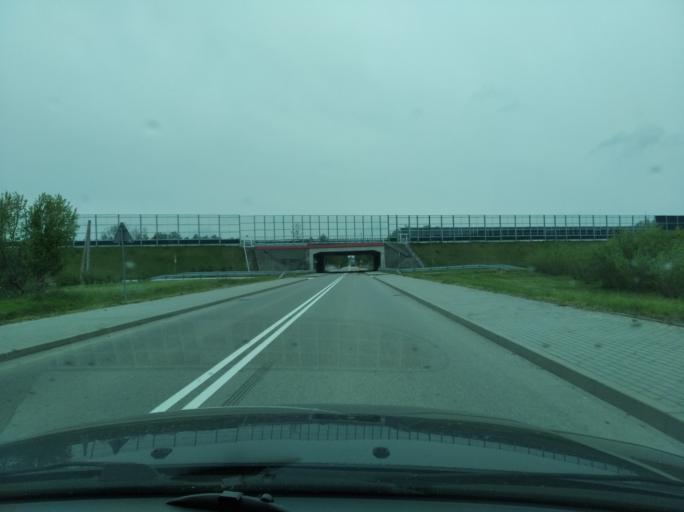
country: PL
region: Subcarpathian Voivodeship
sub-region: Powiat ropczycko-sedziszowski
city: Sedziszow Malopolski
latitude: 50.1136
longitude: 21.7454
